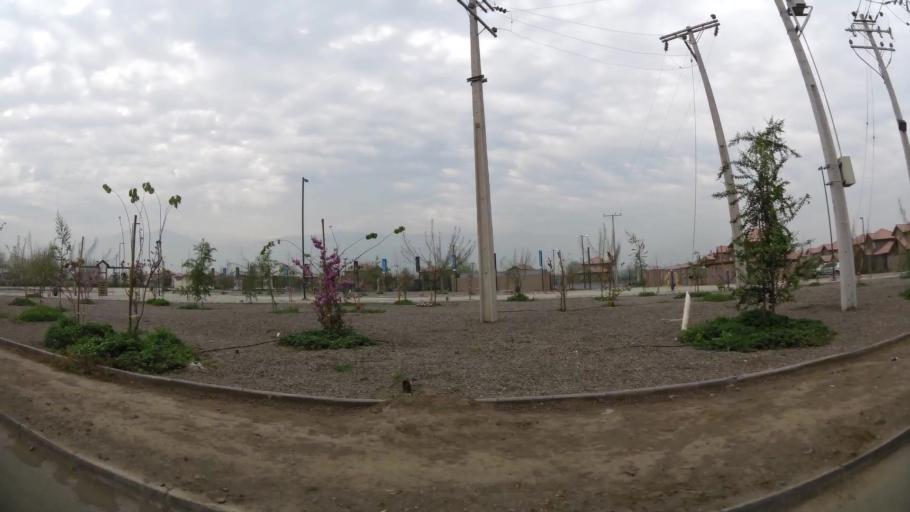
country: CL
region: Santiago Metropolitan
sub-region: Provincia de Chacabuco
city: Chicureo Abajo
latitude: -33.2182
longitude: -70.6757
